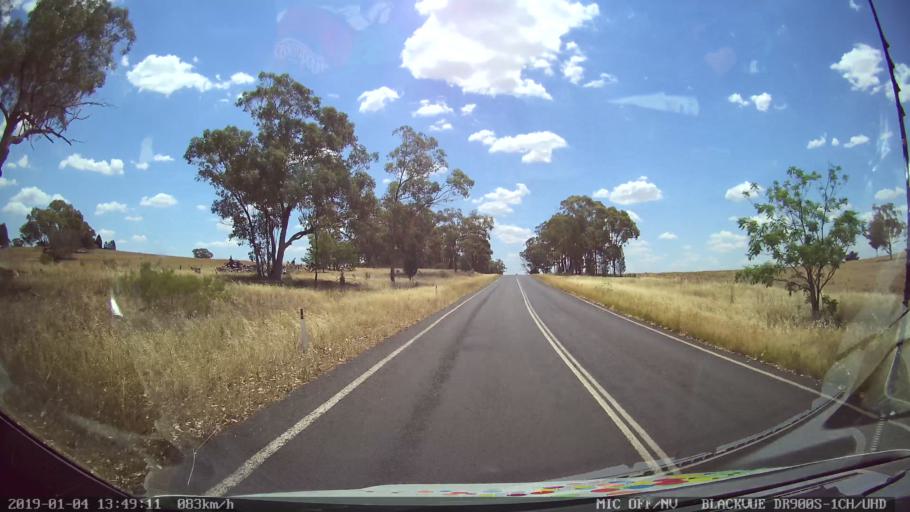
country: AU
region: New South Wales
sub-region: Dubbo Municipality
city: Dubbo
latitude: -32.4351
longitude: 148.5806
